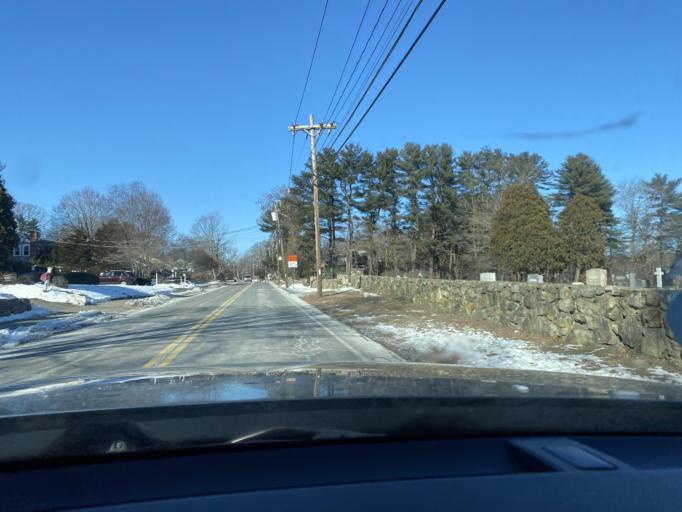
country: US
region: Massachusetts
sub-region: Norfolk County
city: Walpole
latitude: 42.1550
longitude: -71.2500
